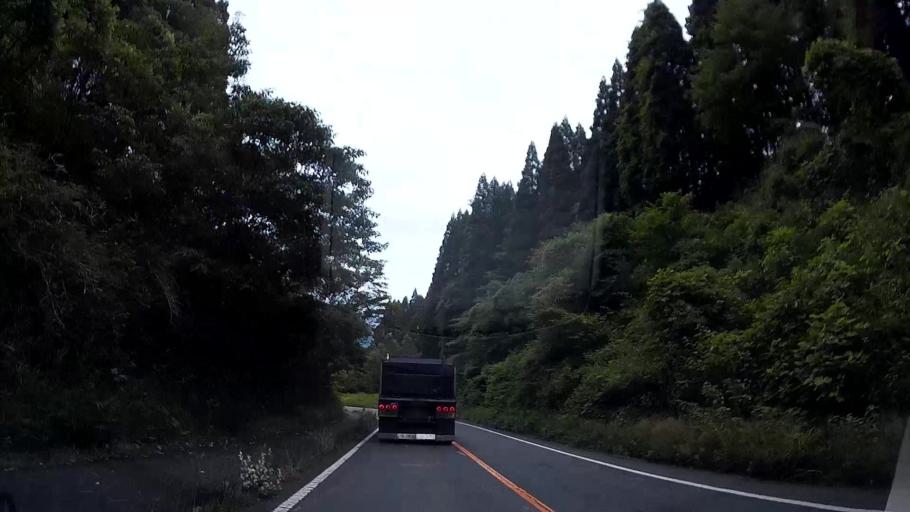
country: JP
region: Oita
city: Tsukawaki
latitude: 33.1239
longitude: 131.0445
